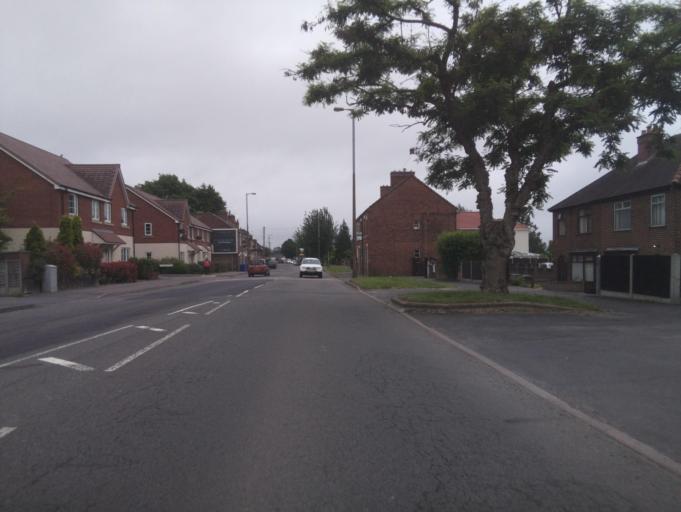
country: GB
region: England
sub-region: Staffordshire
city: Burton upon Trent
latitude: 52.7844
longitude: -1.6143
